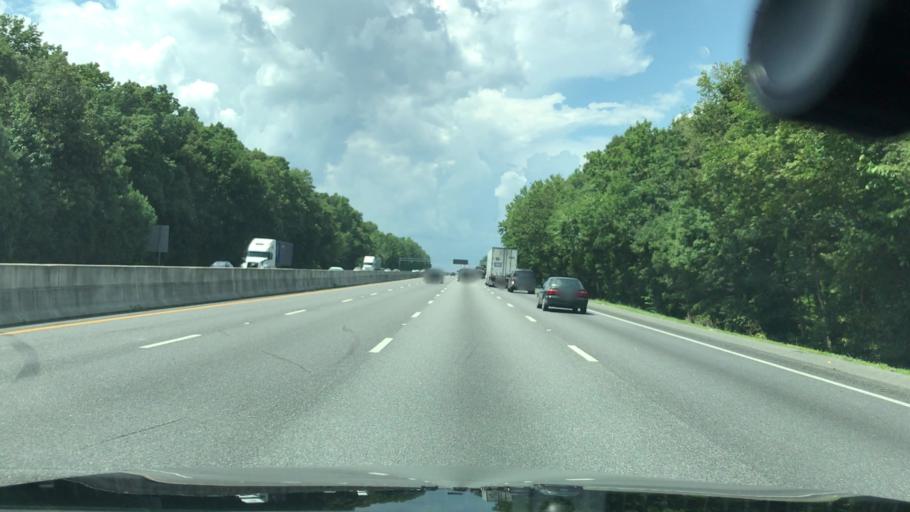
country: US
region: South Carolina
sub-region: York County
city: Rock Hill
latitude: 34.9562
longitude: -80.9791
